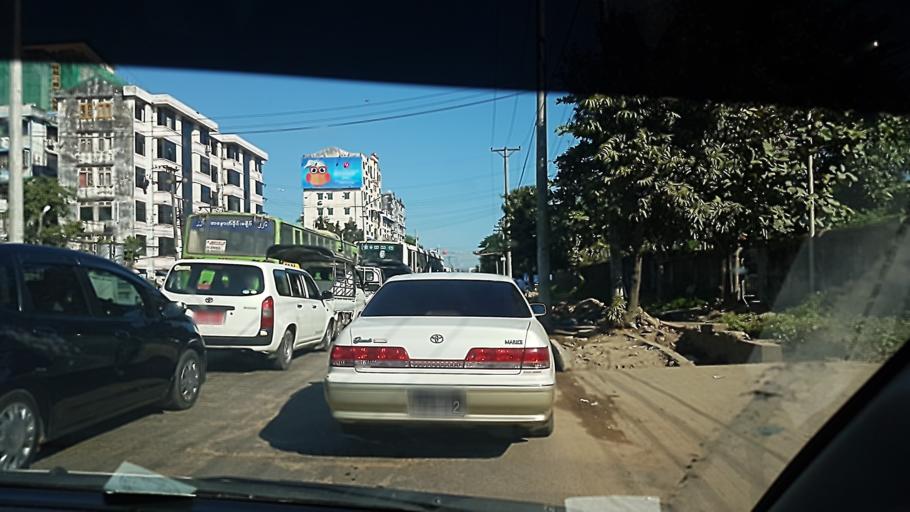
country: MM
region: Yangon
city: Yangon
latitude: 16.8566
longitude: 96.1236
